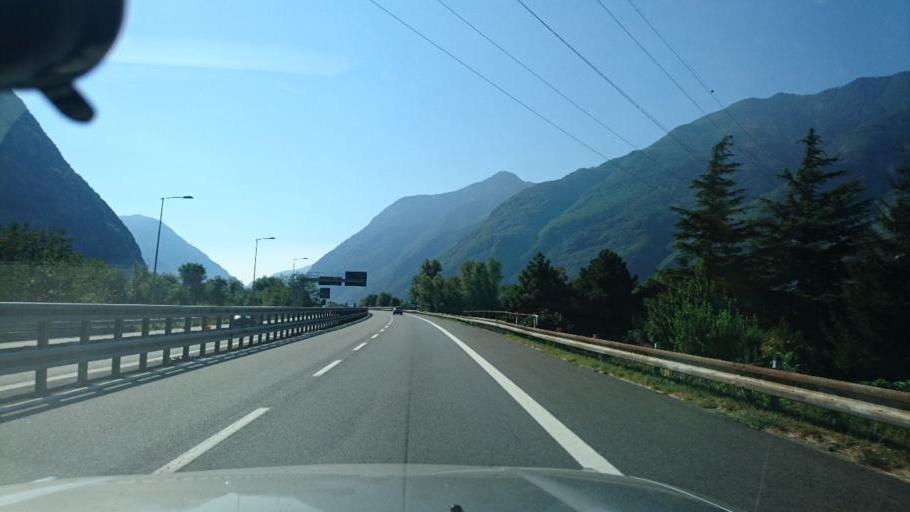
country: IT
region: Aosta Valley
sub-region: Valle d'Aosta
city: Verres
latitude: 45.6667
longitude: 7.6845
